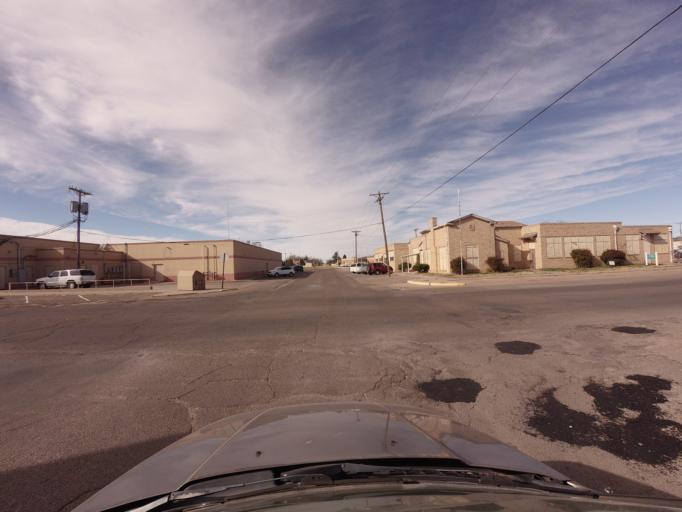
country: US
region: New Mexico
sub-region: Curry County
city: Clovis
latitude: 34.4057
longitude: -103.2039
